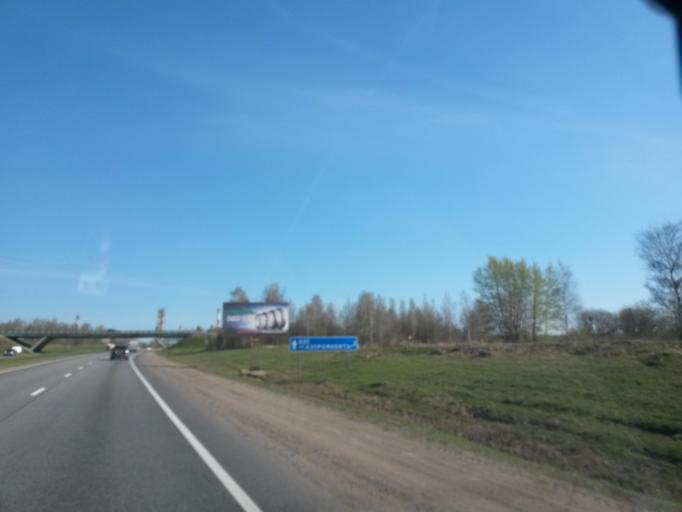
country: RU
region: Jaroslavl
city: Krasnyye Tkachi
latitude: 57.5270
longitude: 39.7836
